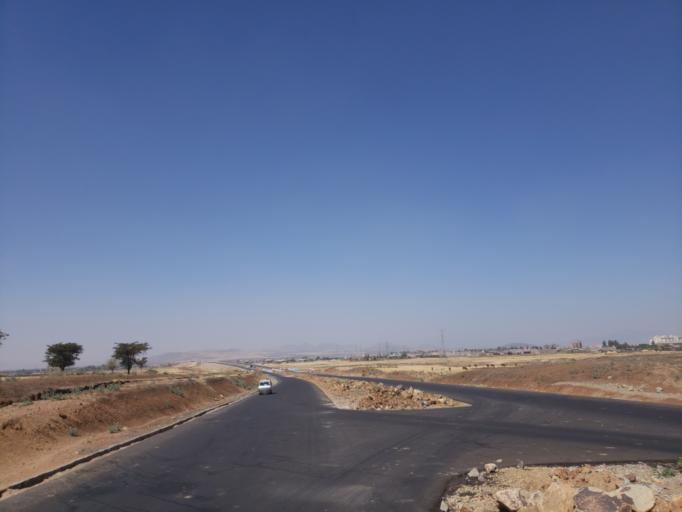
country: ET
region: Oromiya
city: Mojo
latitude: 8.5670
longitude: 39.1504
